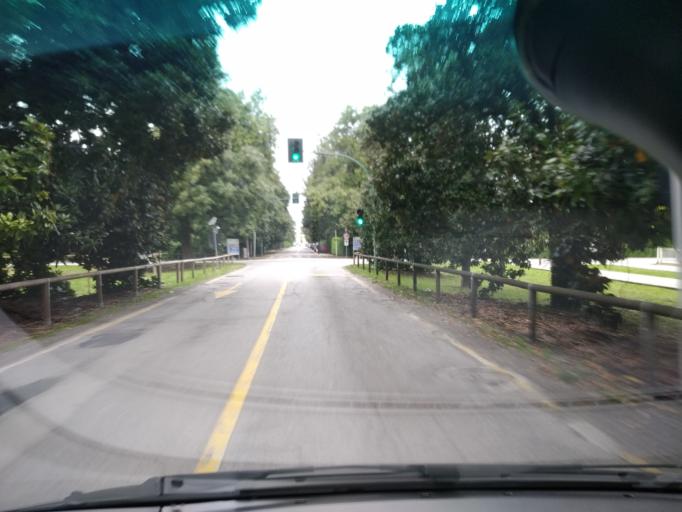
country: IT
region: Veneto
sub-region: Provincia di Padova
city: Piazzola sul Brenta
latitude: 45.5377
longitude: 11.7885
